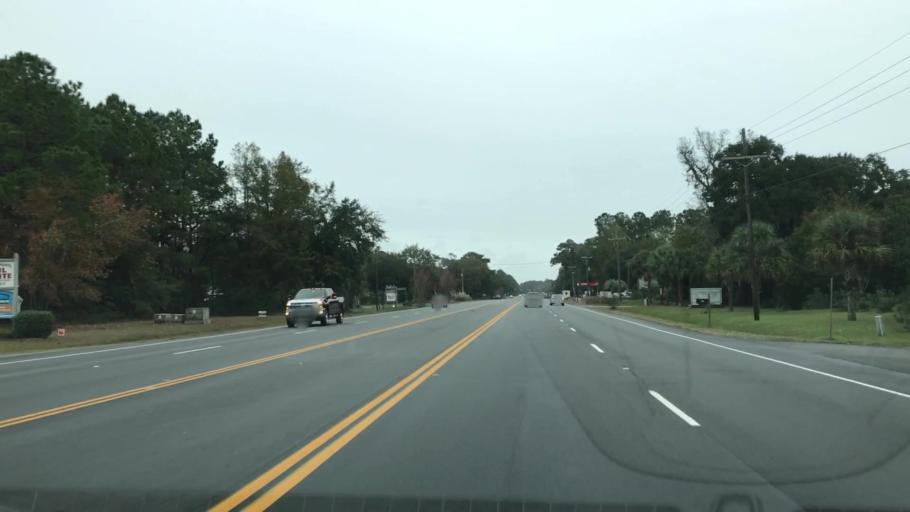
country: US
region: South Carolina
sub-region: Charleston County
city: Awendaw
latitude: 33.0916
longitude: -79.4818
